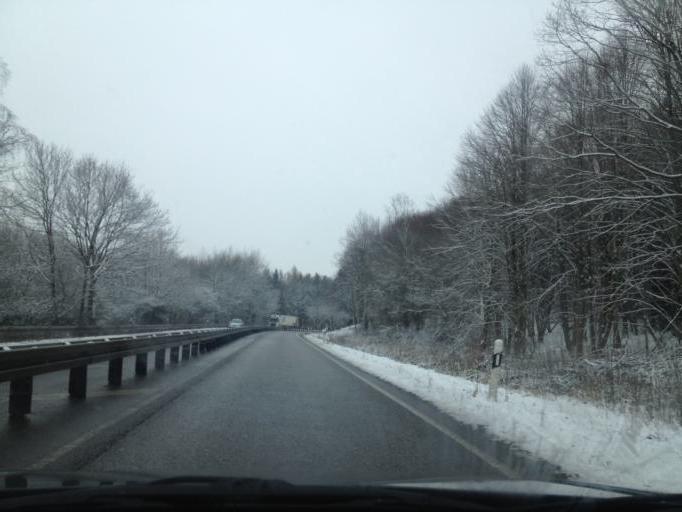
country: DE
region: Saarland
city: Ottweiler
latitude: 49.3889
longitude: 7.1515
